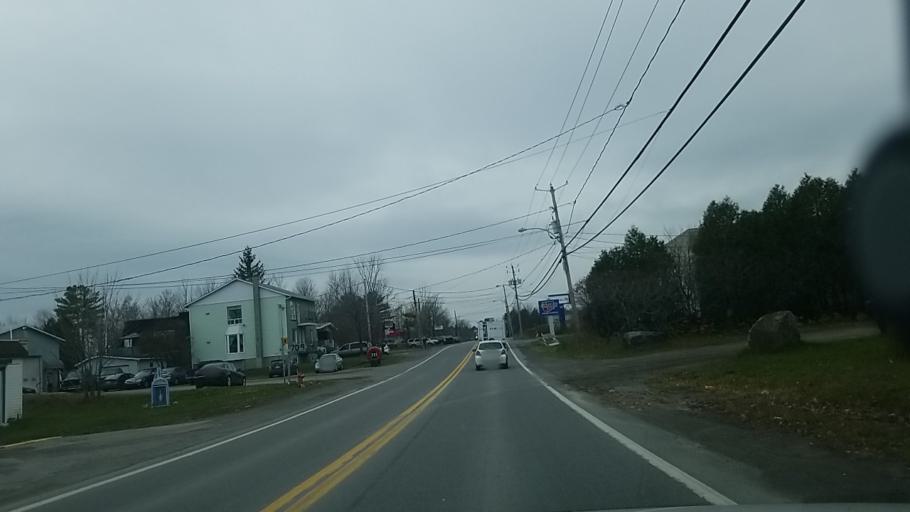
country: CA
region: Quebec
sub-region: Laurentides
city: Saint-Jerome
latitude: 45.7774
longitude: -74.0385
